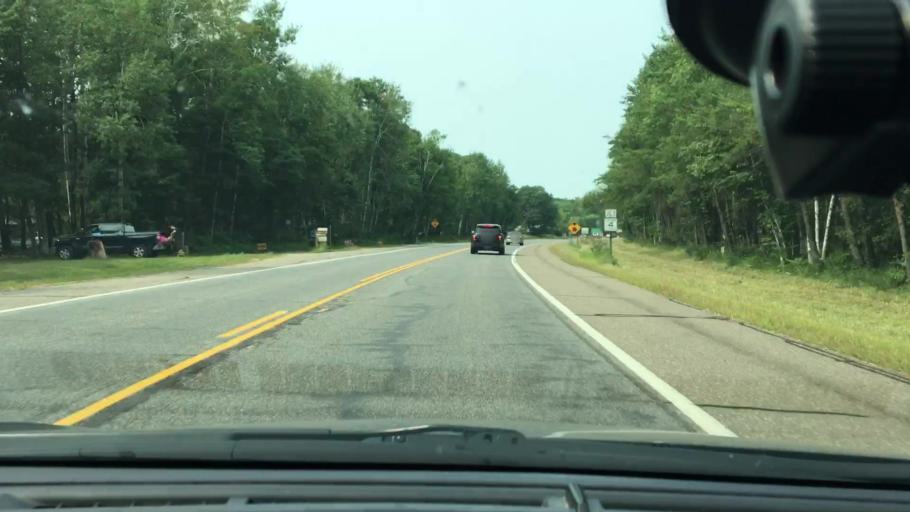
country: US
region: Minnesota
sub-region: Crow Wing County
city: Breezy Point
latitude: 46.4822
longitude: -94.1687
